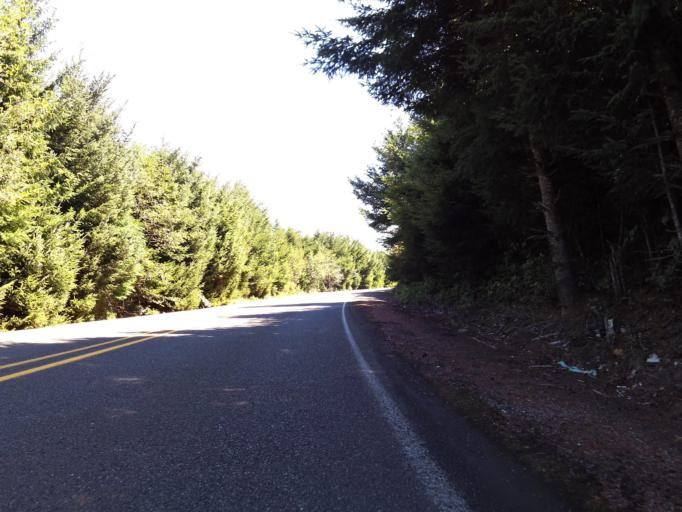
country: US
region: Oregon
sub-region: Coos County
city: Barview
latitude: 43.2710
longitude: -124.3485
